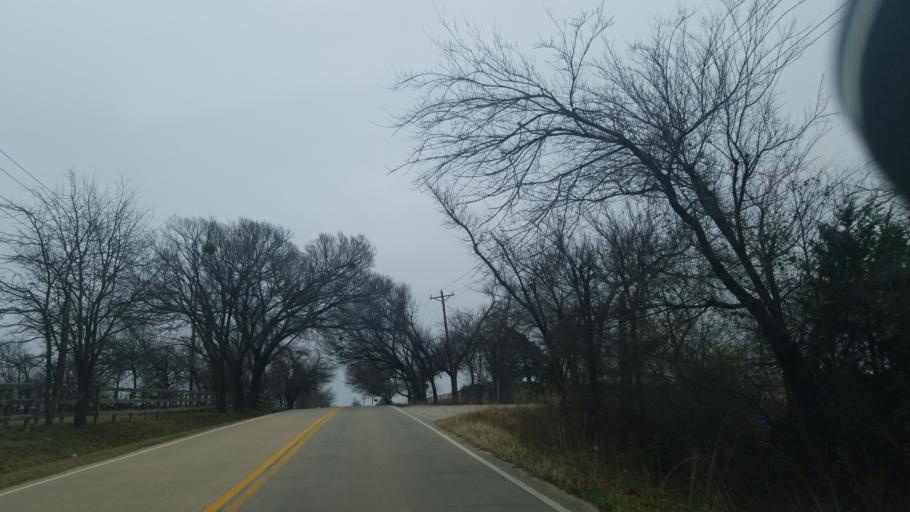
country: US
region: Texas
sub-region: Denton County
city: Copper Canyon
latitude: 33.1178
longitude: -97.1144
